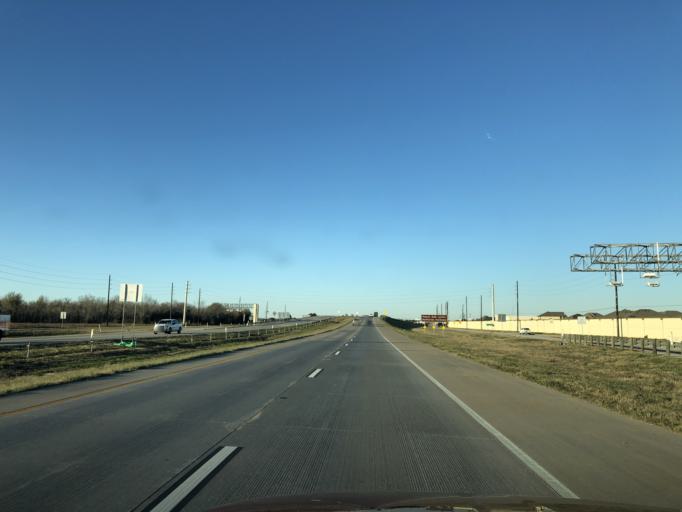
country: US
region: Texas
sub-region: Harris County
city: Cypress
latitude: 30.0106
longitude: -95.7690
